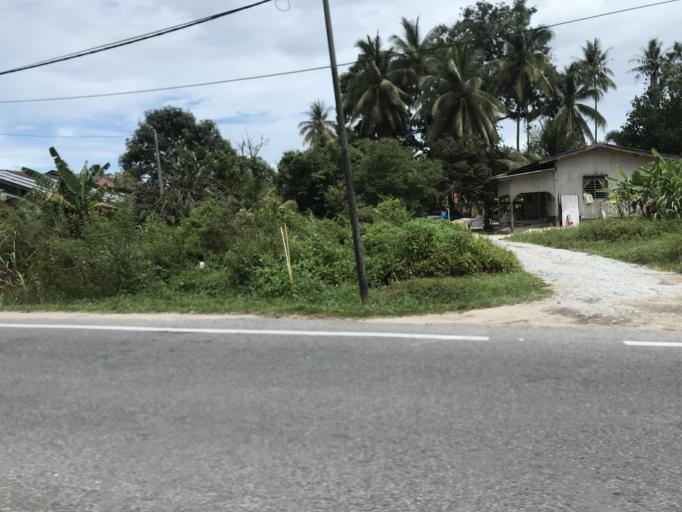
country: MY
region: Kelantan
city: Tumpat
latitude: 6.1751
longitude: 102.1821
